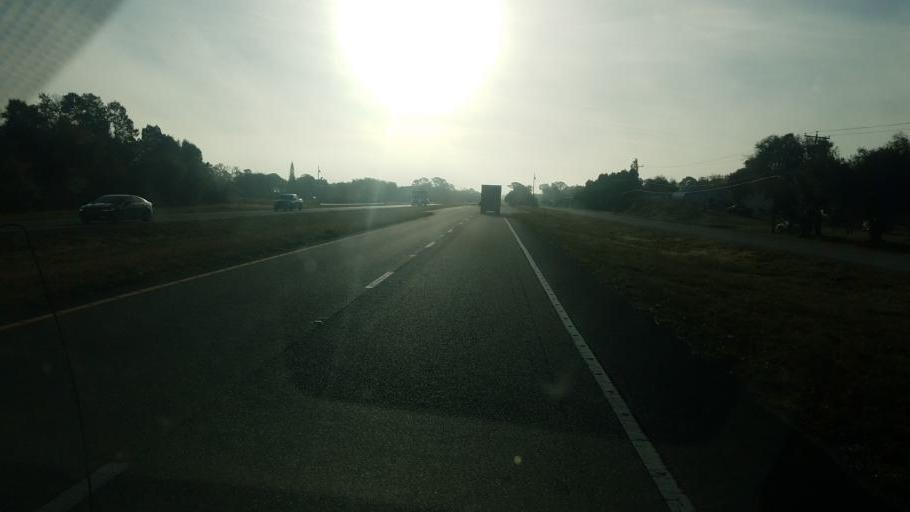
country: US
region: Florida
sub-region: Osceola County
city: Saint Cloud
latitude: 28.2393
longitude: -81.1977
